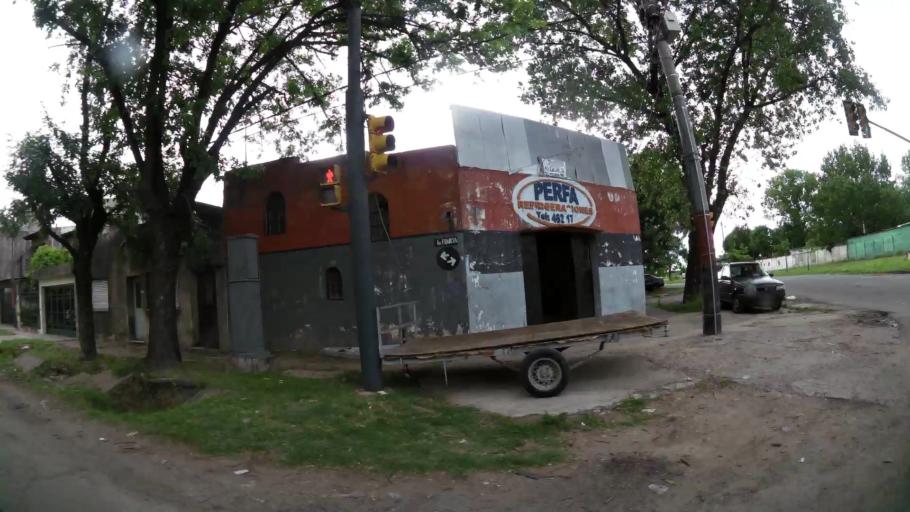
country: AR
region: Santa Fe
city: Gobernador Galvez
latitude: -32.9981
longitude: -60.6780
